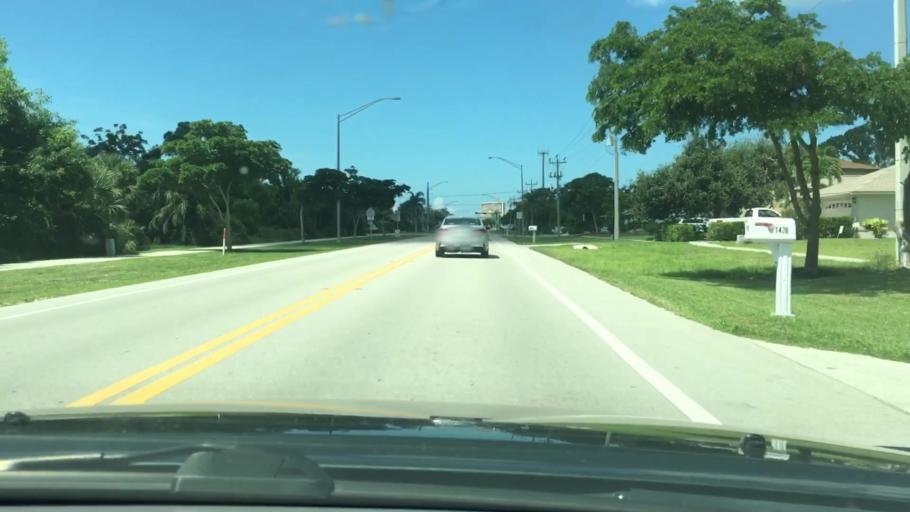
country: US
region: Florida
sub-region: Collier County
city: Marco
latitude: 25.9371
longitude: -81.7112
